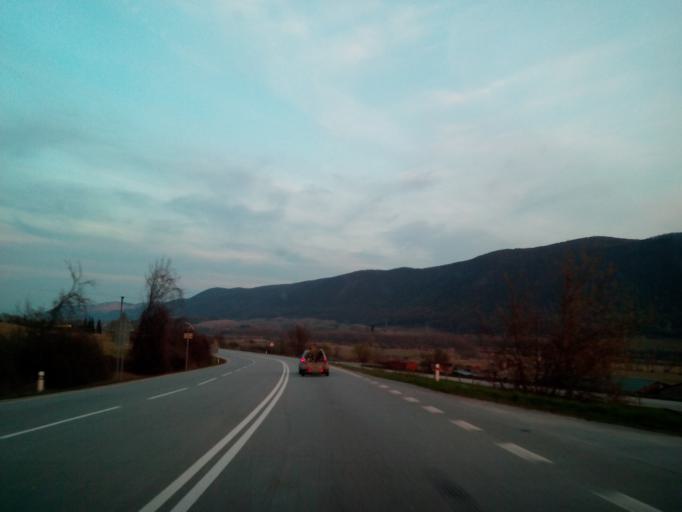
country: SK
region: Kosicky
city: Roznava
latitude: 48.5964
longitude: 20.6811
